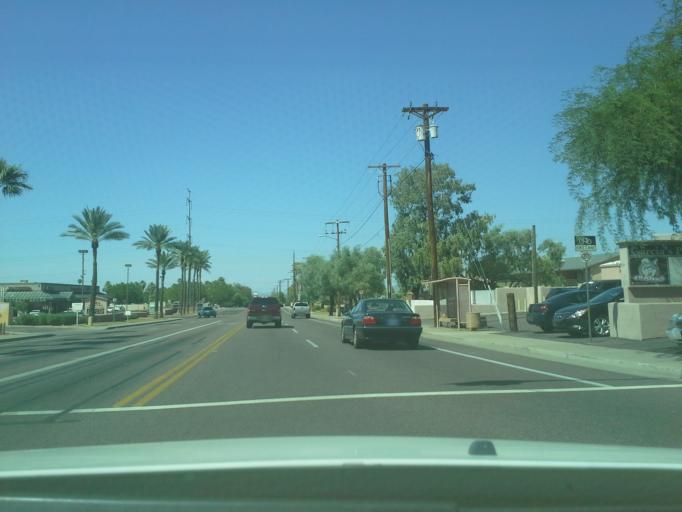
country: US
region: Arizona
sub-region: Maricopa County
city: Phoenix
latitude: 33.3778
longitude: -112.0646
